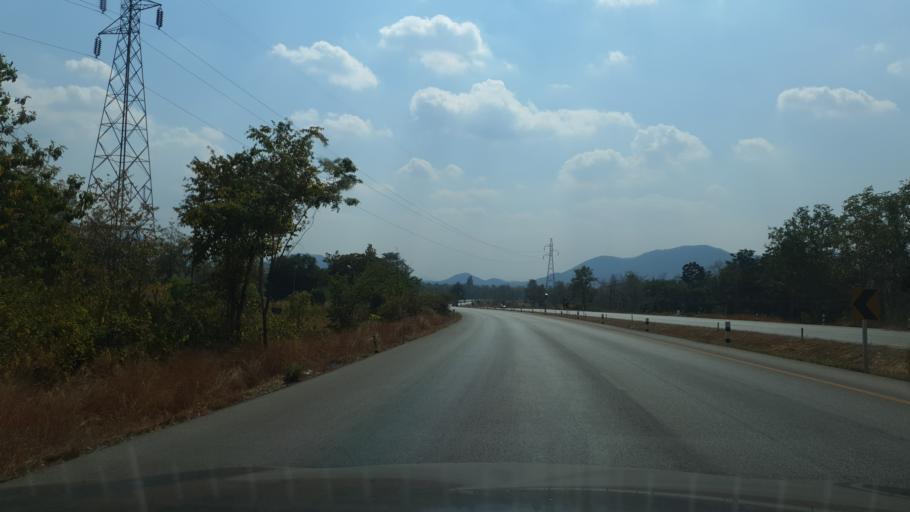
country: TH
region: Lampang
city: Mae Phrik
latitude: 17.3822
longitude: 99.1481
